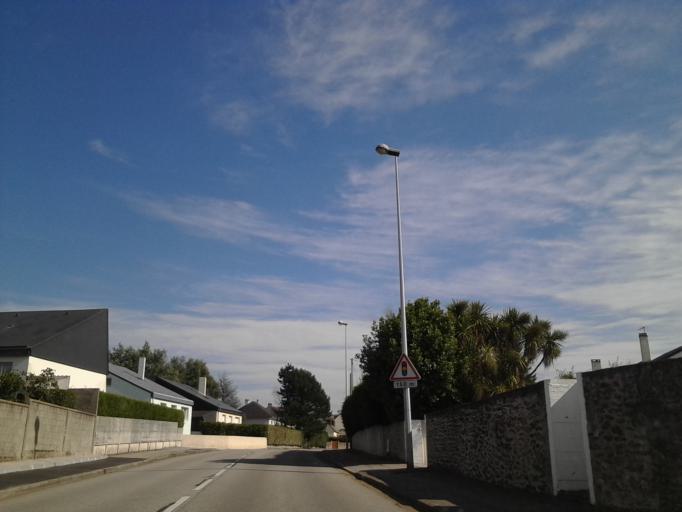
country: FR
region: Lower Normandy
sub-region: Departement de la Manche
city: Tourlaville
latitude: 49.6418
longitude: -1.5736
